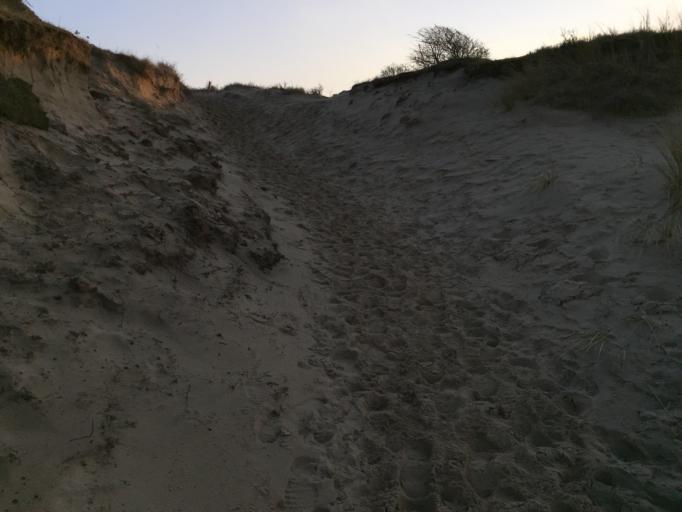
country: NL
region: South Holland
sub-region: Gemeente Katwijk
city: Katwijk aan Zee
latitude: 52.1741
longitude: 4.3705
